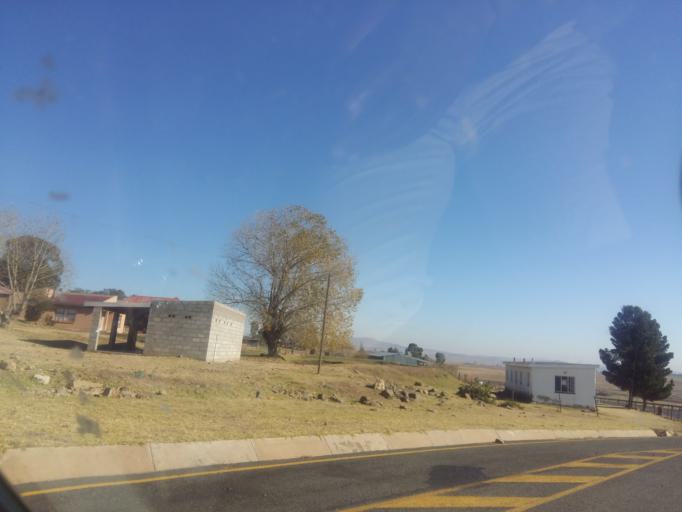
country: LS
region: Mafeteng
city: Mafeteng
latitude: -29.6825
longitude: 27.2819
